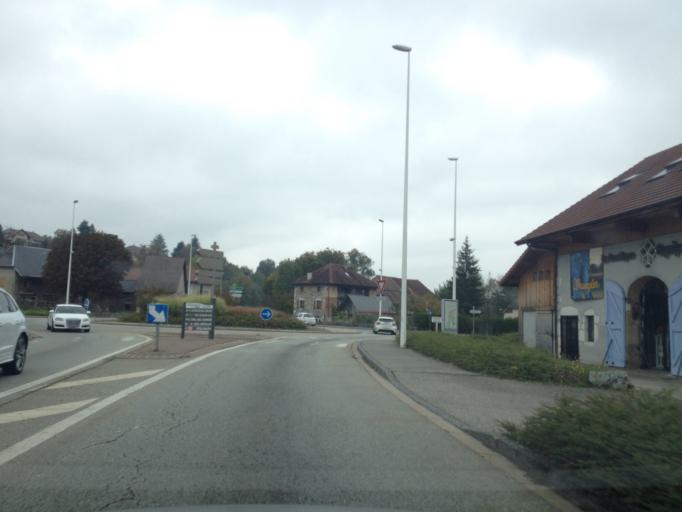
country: FR
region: Rhone-Alpes
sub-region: Departement de la Haute-Savoie
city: Seynod
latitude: 45.8632
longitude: 6.0686
